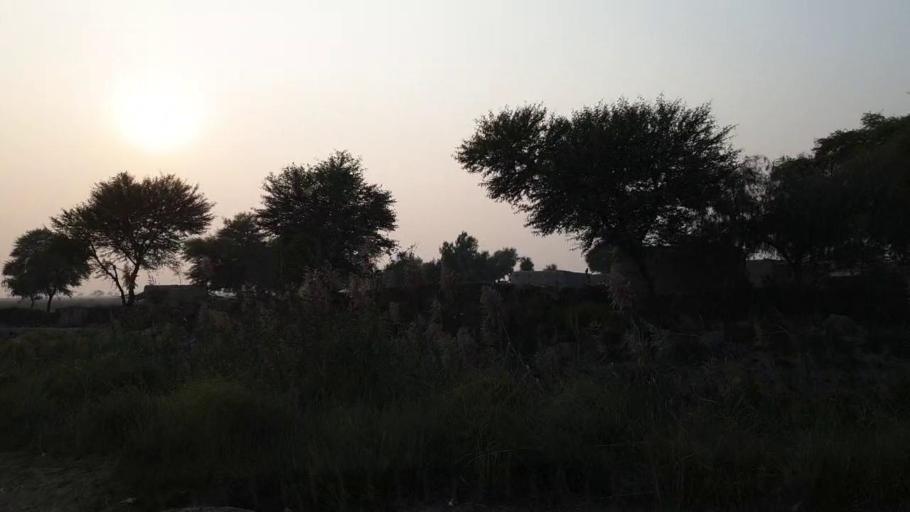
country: PK
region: Sindh
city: Bhan
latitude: 26.5048
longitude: 67.7114
